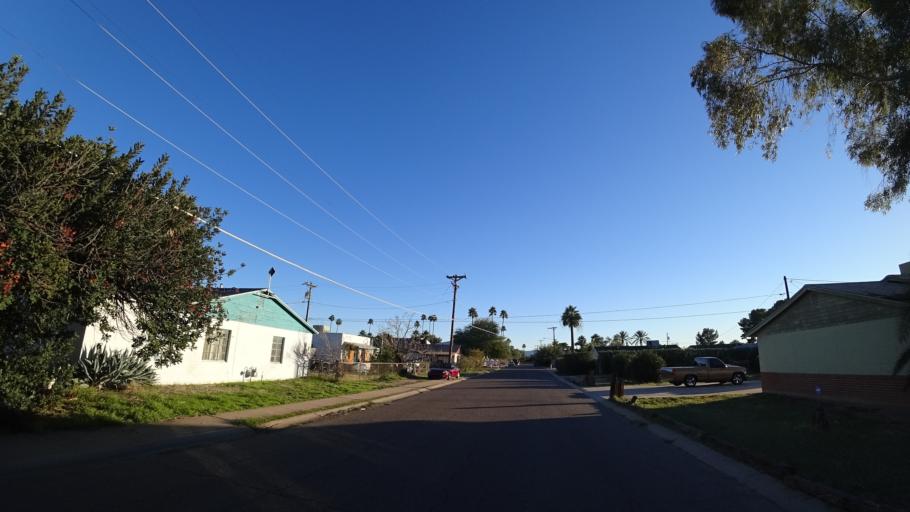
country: US
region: Arizona
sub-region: Maricopa County
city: Phoenix
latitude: 33.4866
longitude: -112.0324
